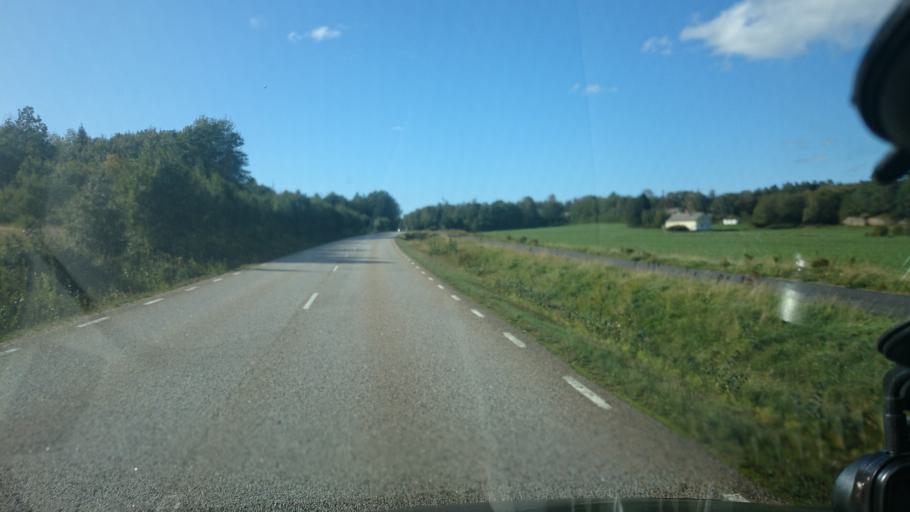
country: SE
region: Vaestra Goetaland
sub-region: Lysekils Kommun
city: Brastad
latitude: 58.3319
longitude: 11.4533
